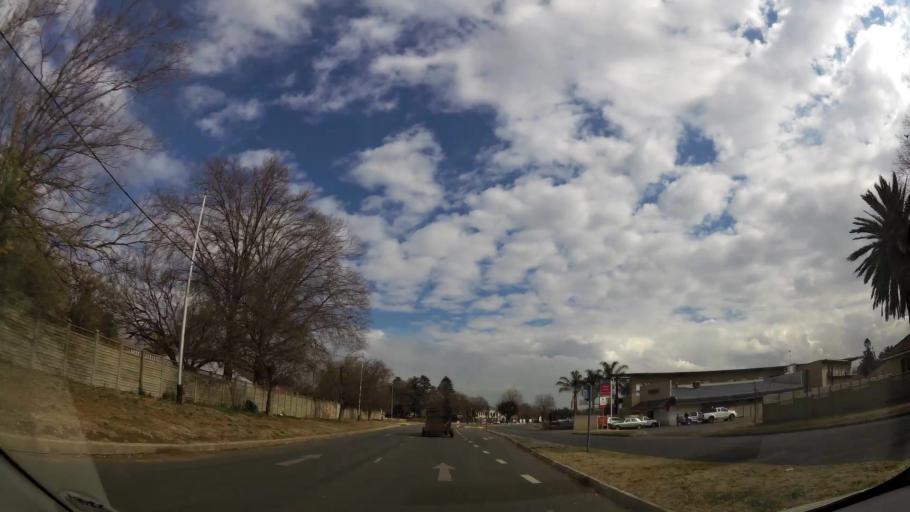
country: ZA
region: Gauteng
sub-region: Sedibeng District Municipality
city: Vereeniging
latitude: -26.6614
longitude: 27.9795
